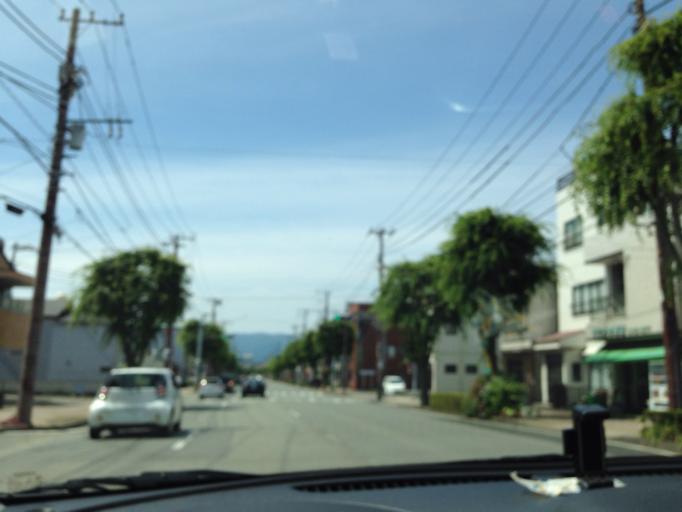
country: JP
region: Shizuoka
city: Numazu
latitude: 35.0933
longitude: 138.8570
